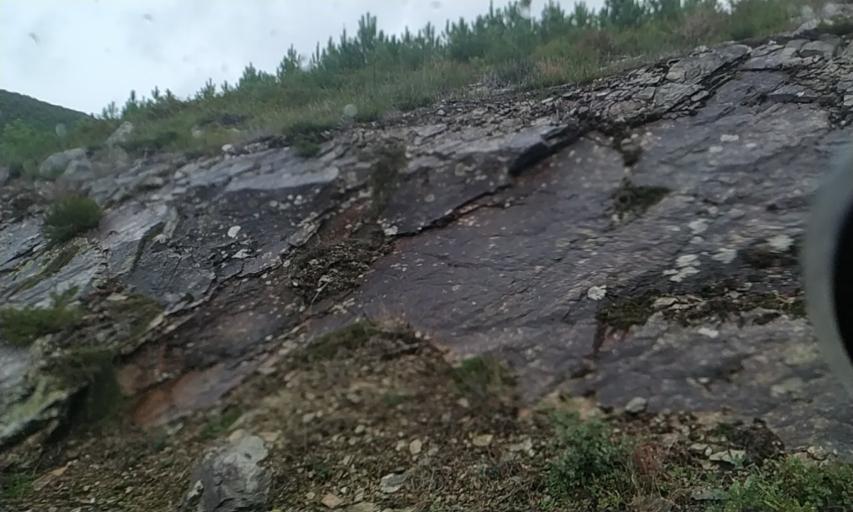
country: PT
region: Vila Real
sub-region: Mondim de Basto
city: Mondim de Basto
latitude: 41.3538
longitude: -7.9081
